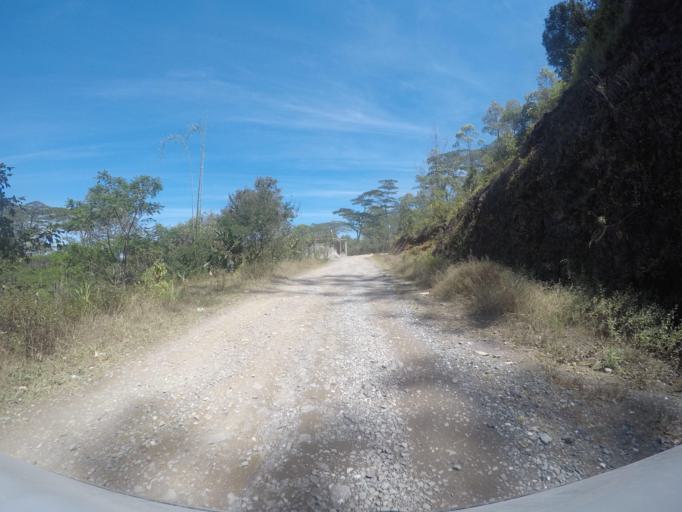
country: TL
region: Ermera
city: Gleno
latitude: -8.7865
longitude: 125.3787
